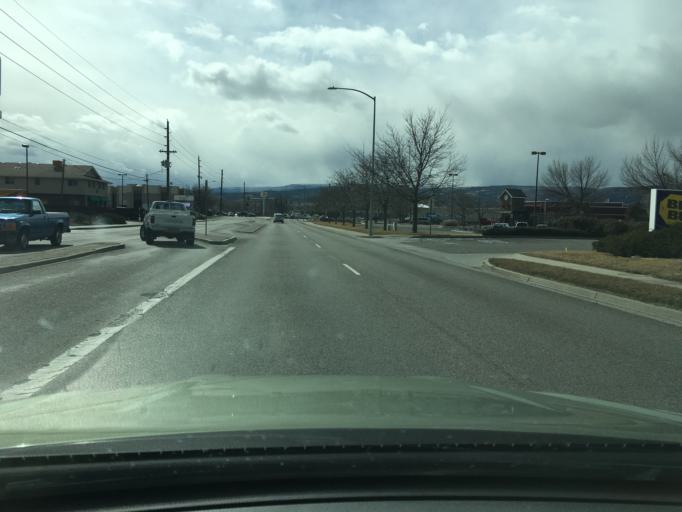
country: US
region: Colorado
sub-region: Mesa County
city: Redlands
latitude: 39.0894
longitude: -108.5988
